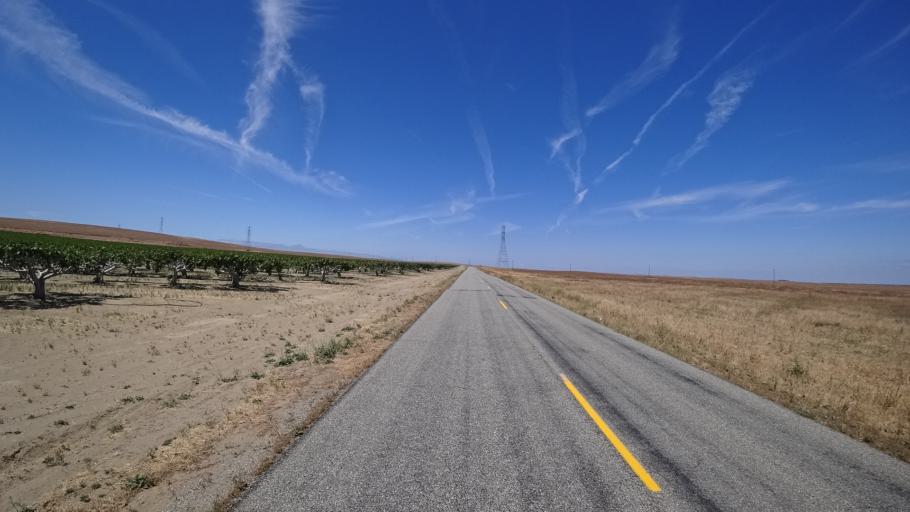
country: US
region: California
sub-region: Kings County
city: Kettleman City
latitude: 35.7849
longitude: -119.8825
